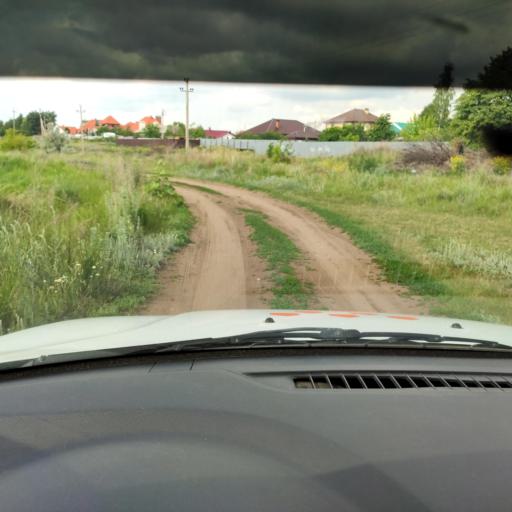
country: RU
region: Samara
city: Podstepki
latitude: 53.6132
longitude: 49.0328
